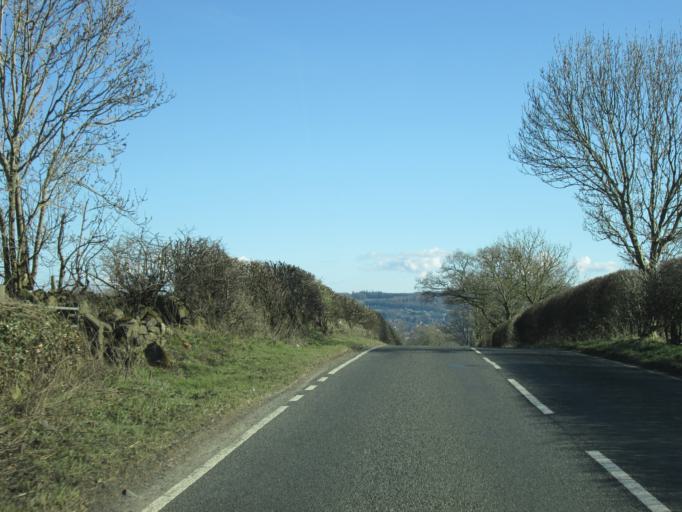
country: GB
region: England
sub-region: Northumberland
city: Acomb
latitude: 54.9983
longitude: -2.1215
